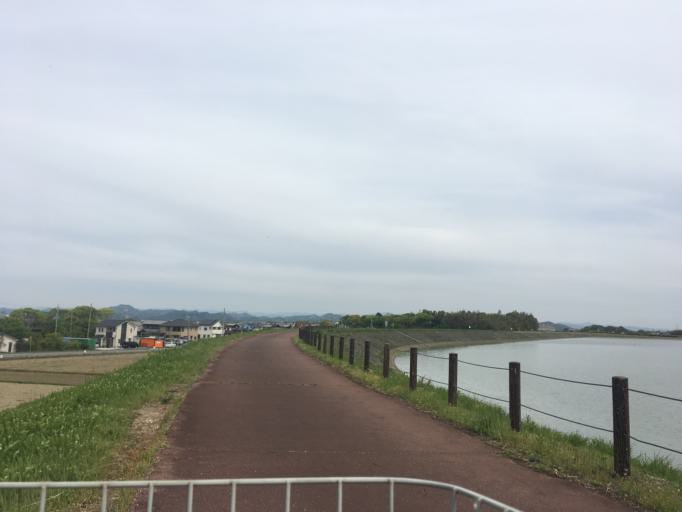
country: JP
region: Hyogo
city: Miki
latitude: 34.7625
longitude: 134.9208
